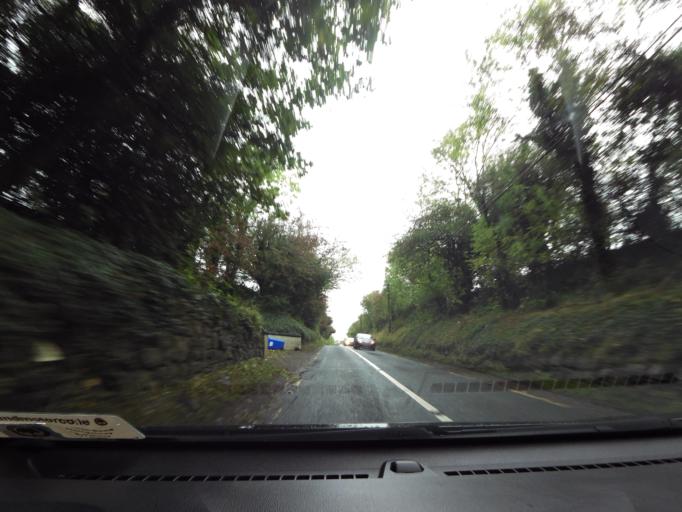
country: IE
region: Connaught
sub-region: County Galway
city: Tuam
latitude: 53.5812
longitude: -8.7811
